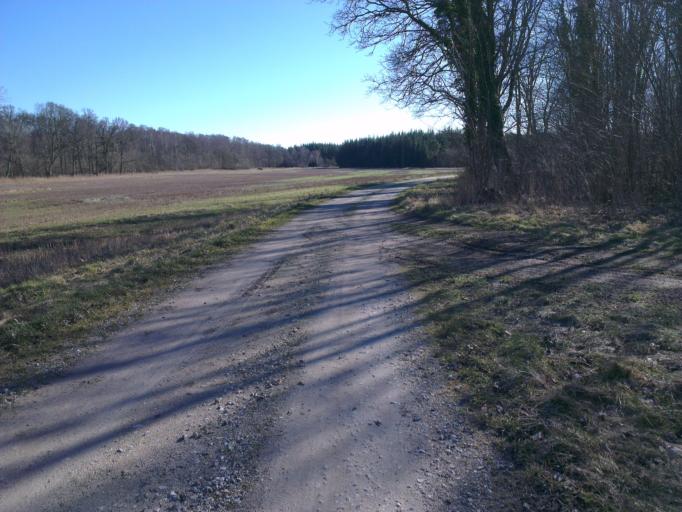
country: DK
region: Capital Region
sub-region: Frederikssund Kommune
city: Jaegerspris
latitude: 55.8917
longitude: 11.9921
